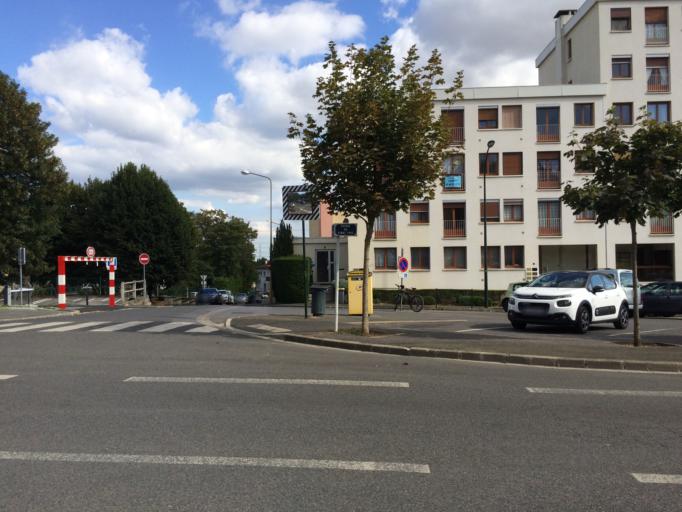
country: FR
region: Ile-de-France
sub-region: Departement de l'Essonne
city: Palaiseau
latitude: 48.7134
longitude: 2.2467
